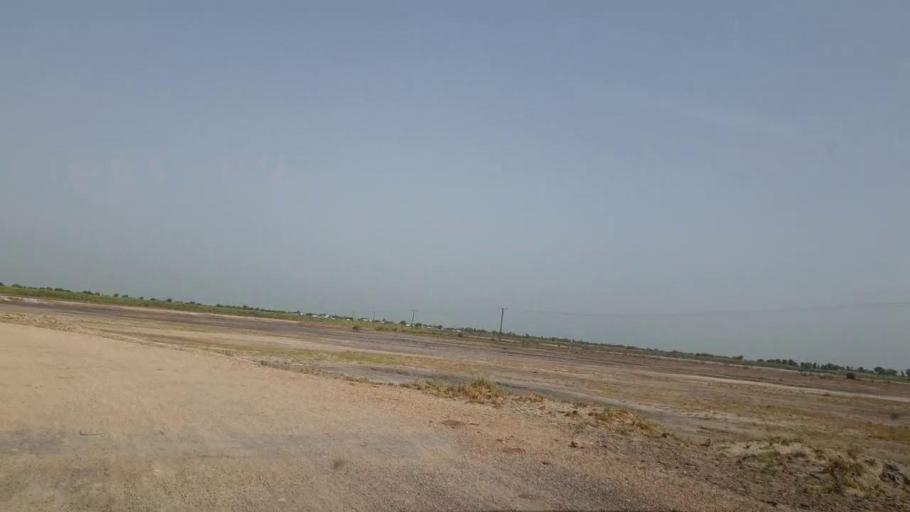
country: PK
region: Sindh
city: Sakrand
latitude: 26.2983
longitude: 68.2214
